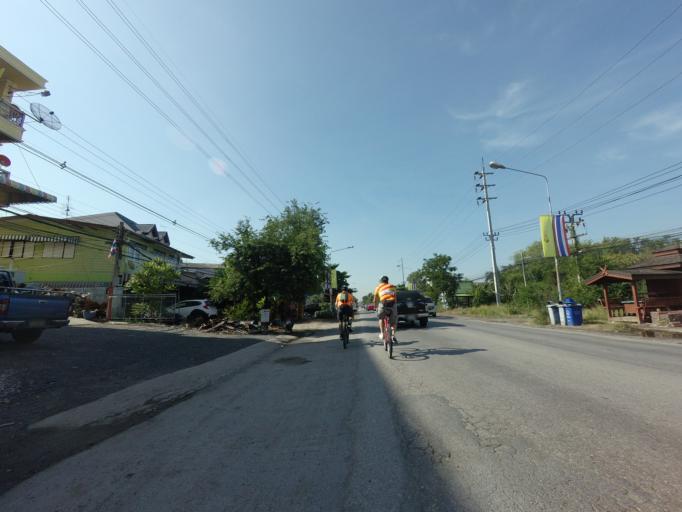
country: TH
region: Samut Prakan
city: Phra Samut Chedi
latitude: 13.5843
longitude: 100.5795
